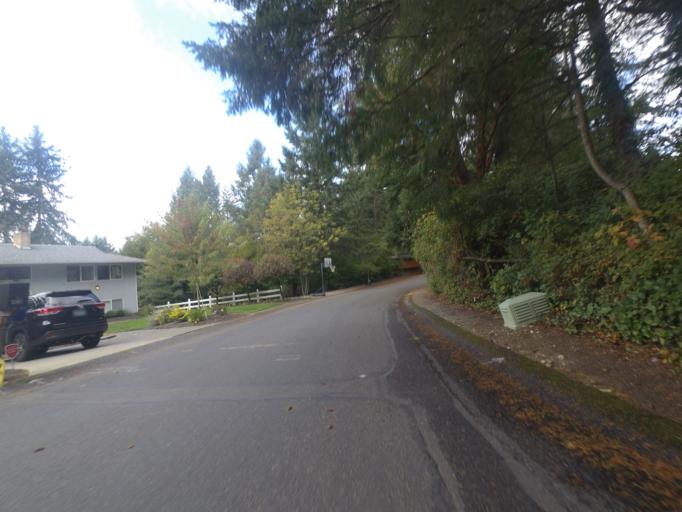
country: US
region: Washington
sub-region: Pierce County
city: University Place
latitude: 47.2141
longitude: -122.5531
